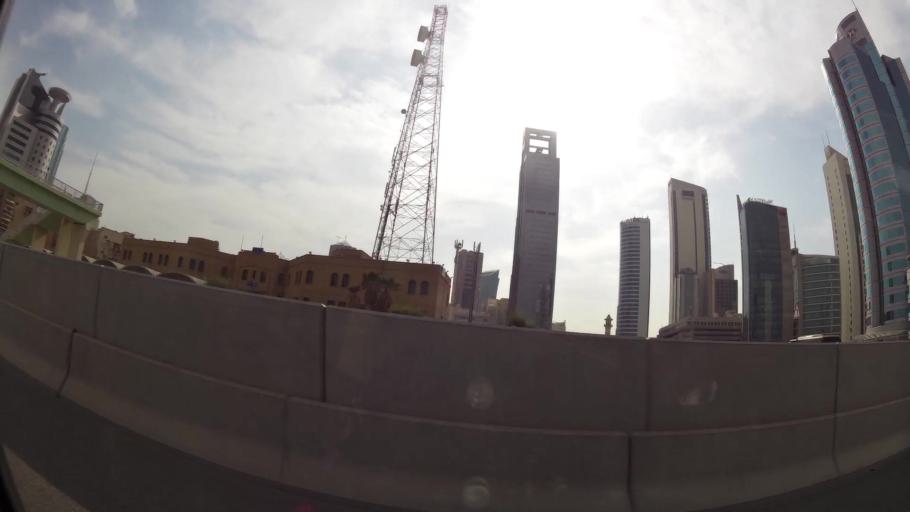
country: KW
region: Al Asimah
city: Kuwait City
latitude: 29.3649
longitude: 47.9615
